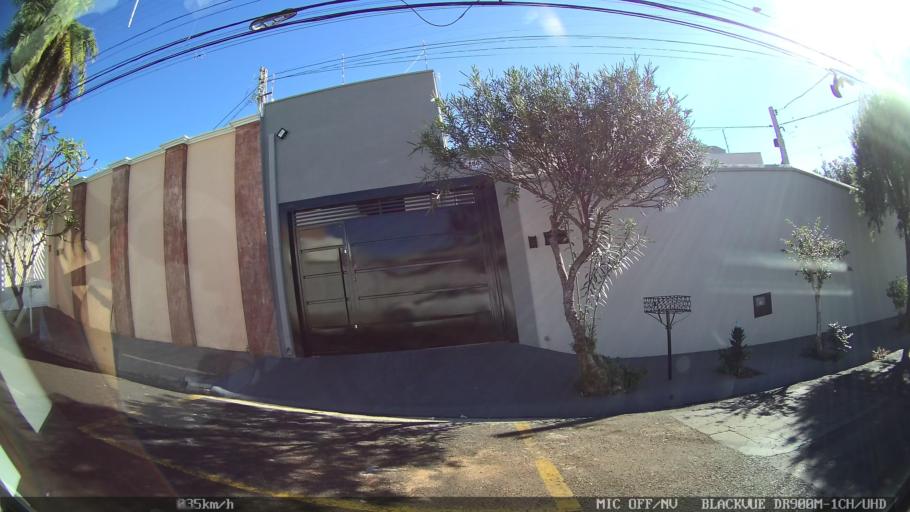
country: BR
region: Sao Paulo
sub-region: Franca
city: Franca
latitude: -20.5417
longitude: -47.4095
